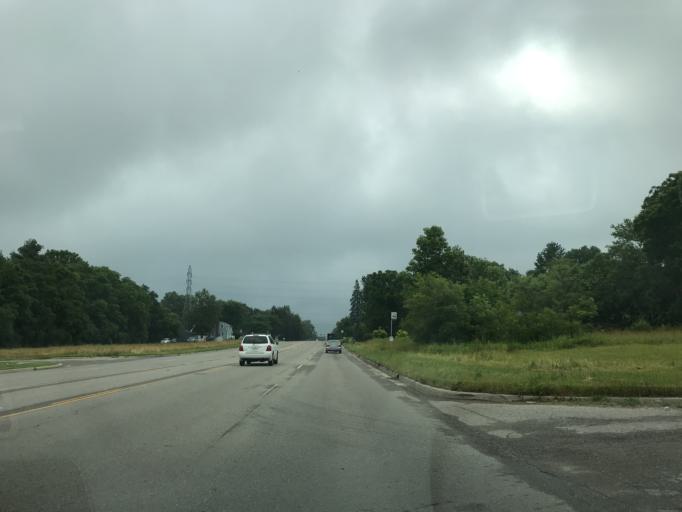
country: US
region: Michigan
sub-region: Washtenaw County
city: Ypsilanti
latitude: 42.2450
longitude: -83.6548
